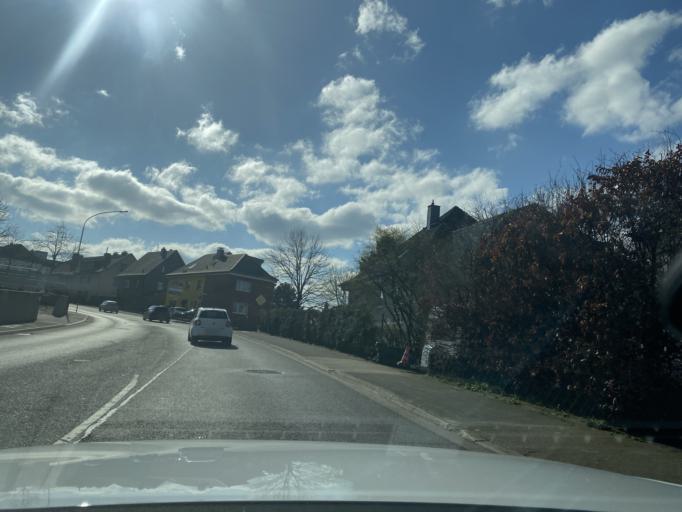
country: DE
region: North Rhine-Westphalia
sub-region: Regierungsbezirk Koln
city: Bergisch Gladbach
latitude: 50.9666
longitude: 7.1512
